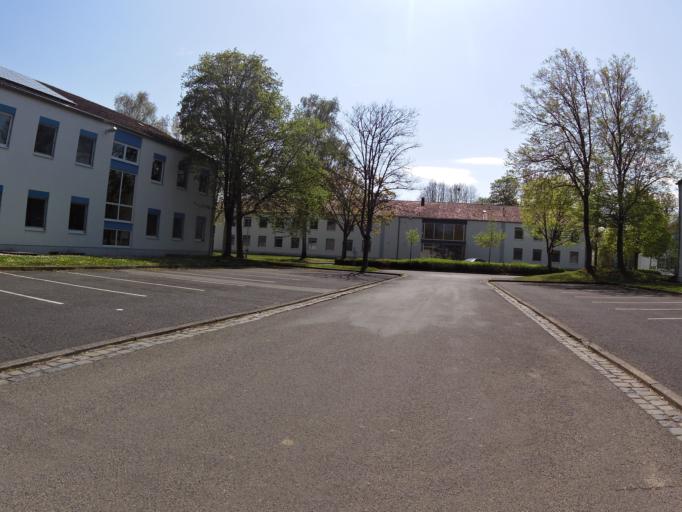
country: DE
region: Bavaria
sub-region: Regierungsbezirk Unterfranken
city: Giebelstadt
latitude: 49.6886
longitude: 9.9517
